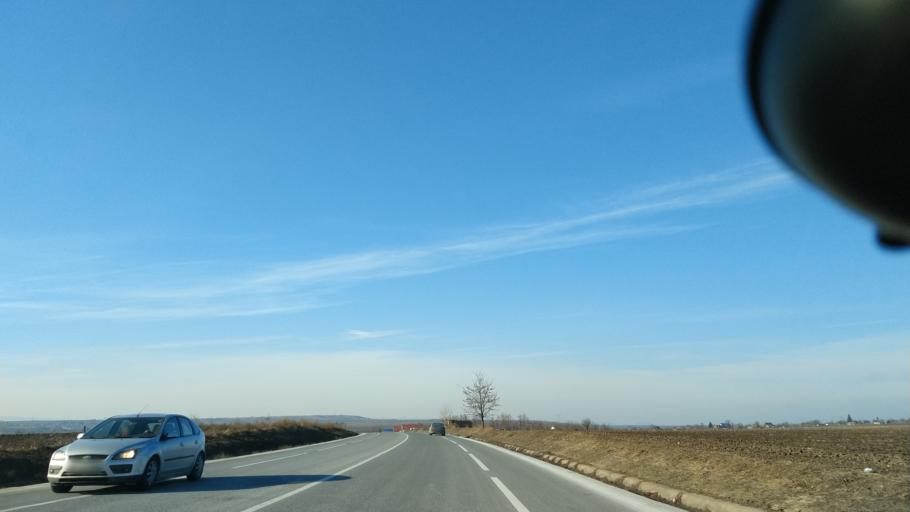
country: RO
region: Iasi
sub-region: Comuna Podu Iloaiei
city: Budai
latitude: 47.2238
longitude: 27.1929
